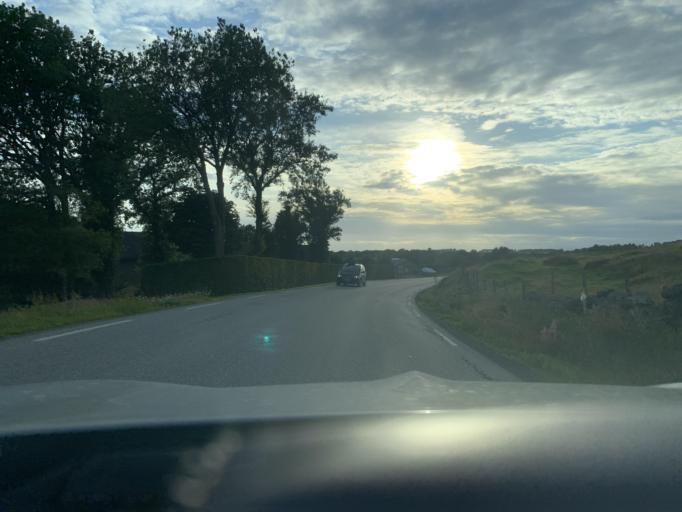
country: NO
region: Rogaland
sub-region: Ha
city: Naerbo
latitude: 58.6851
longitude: 5.7348
